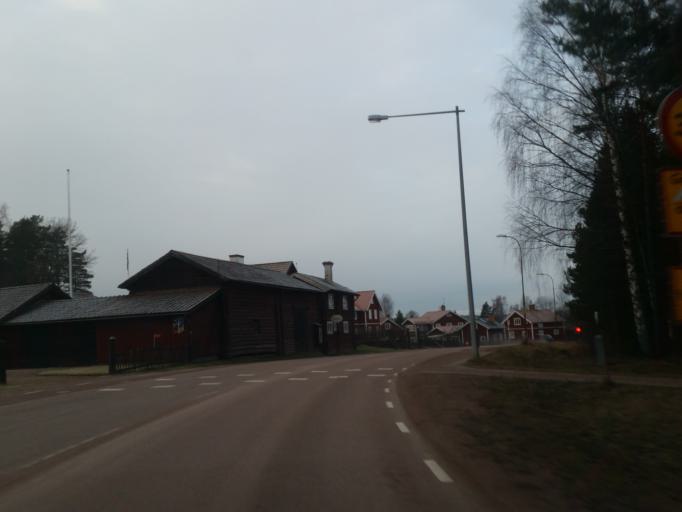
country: SE
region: Dalarna
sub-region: Leksand Municipality
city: Leksand
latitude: 60.7207
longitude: 15.0065
